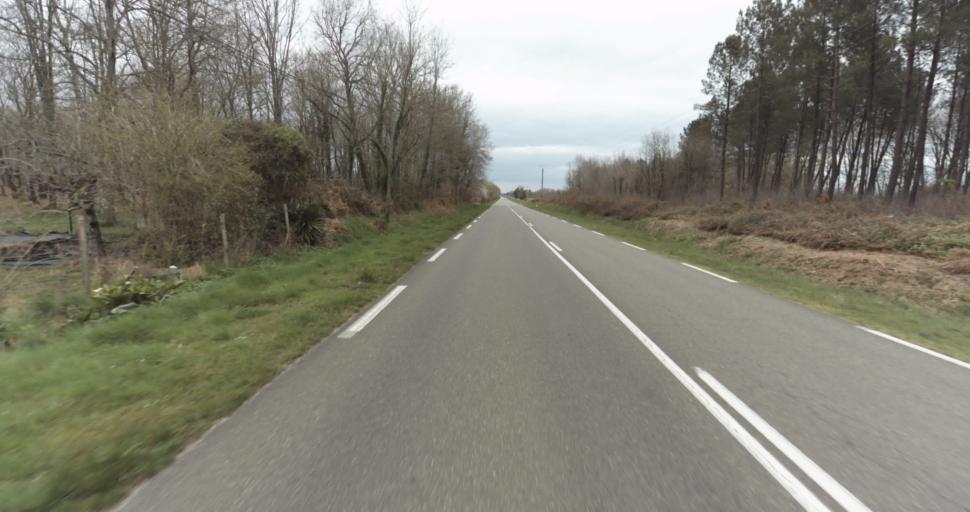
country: FR
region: Aquitaine
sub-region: Departement des Landes
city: Sarbazan
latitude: 44.0100
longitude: -0.3238
